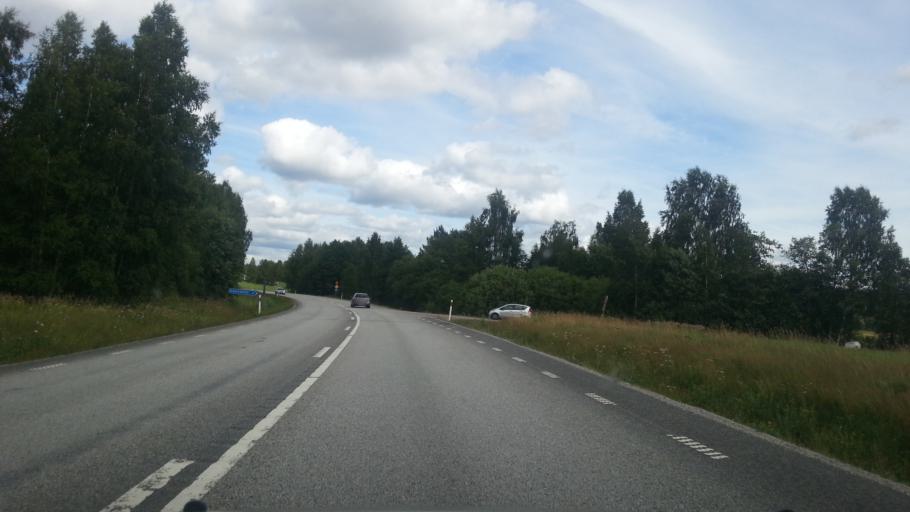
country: SE
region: OErebro
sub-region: Lindesbergs Kommun
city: Lindesberg
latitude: 59.6274
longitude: 15.2149
